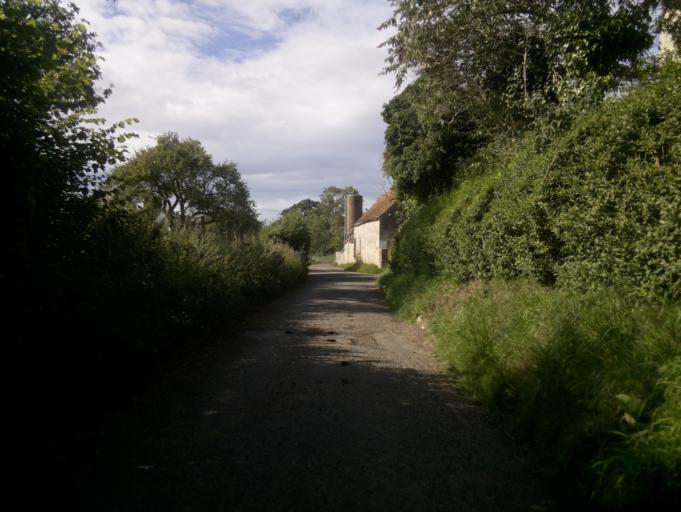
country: GB
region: England
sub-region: Gloucestershire
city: Painswick
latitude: 51.7928
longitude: -2.2437
